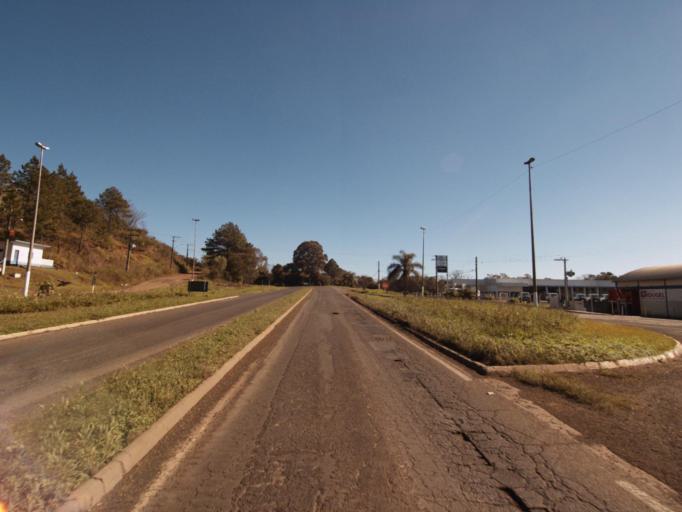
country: BR
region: Santa Catarina
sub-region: Joacaba
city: Joacaba
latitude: -27.1766
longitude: -51.5257
